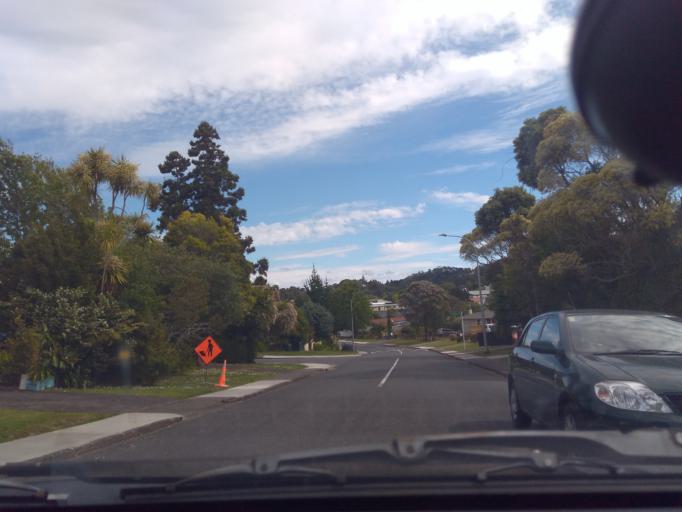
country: NZ
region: Auckland
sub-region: Auckland
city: Waitakere
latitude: -36.9270
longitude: 174.6721
